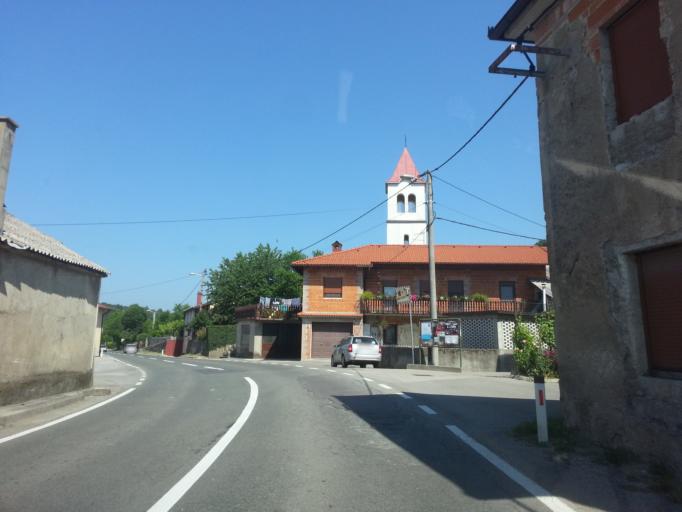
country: SI
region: Ilirska Bistrica
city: Ilirska Bistrica
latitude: 45.5058
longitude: 14.2671
